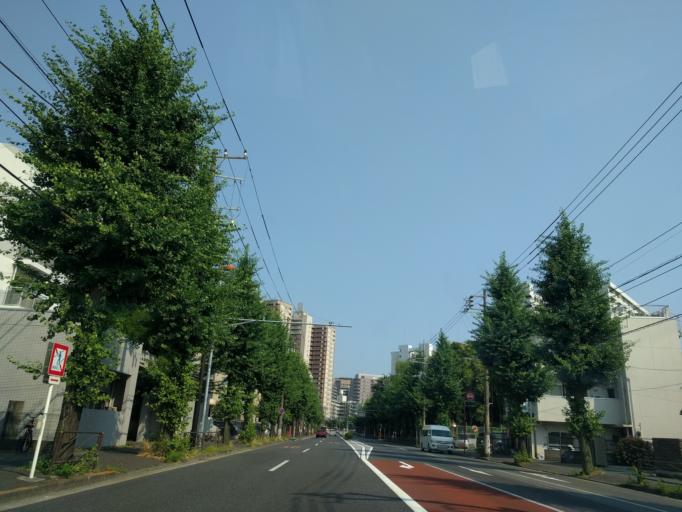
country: JP
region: Kanagawa
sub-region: Kawasaki-shi
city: Kawasaki
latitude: 35.5419
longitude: 139.6949
